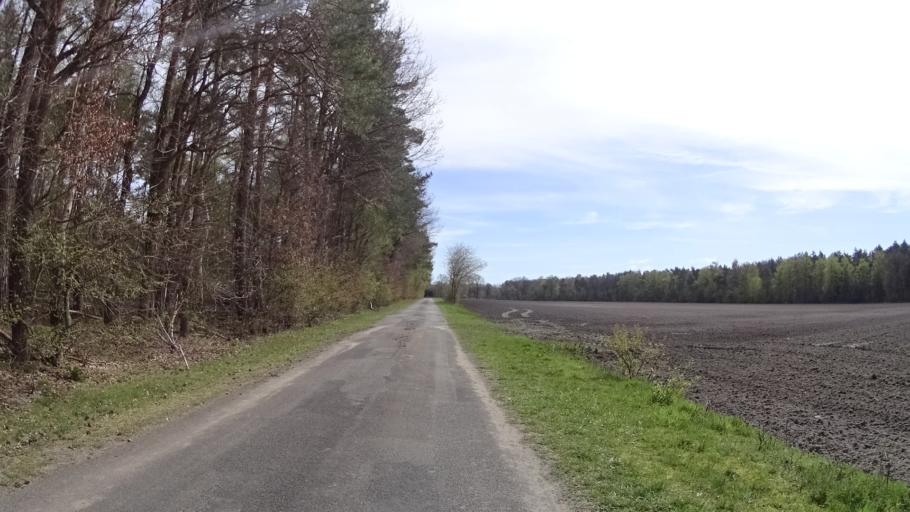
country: DE
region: Lower Saxony
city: Lunne
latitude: 52.3789
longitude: 7.3993
